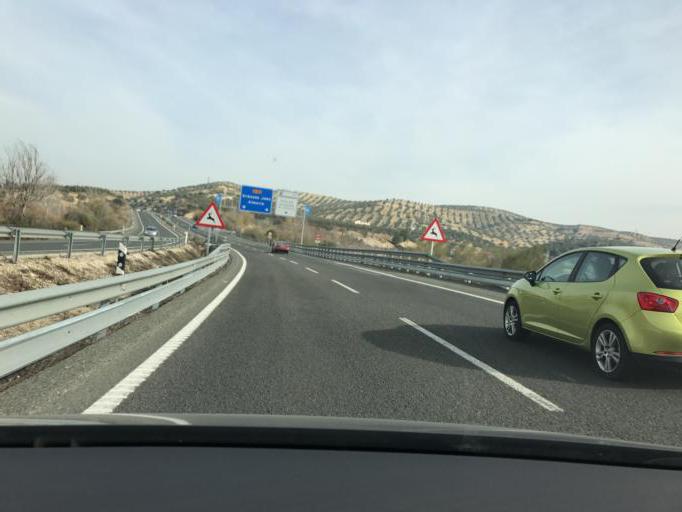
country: ES
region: Andalusia
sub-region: Provincia de Granada
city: Salar
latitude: 37.1670
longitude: -4.0878
